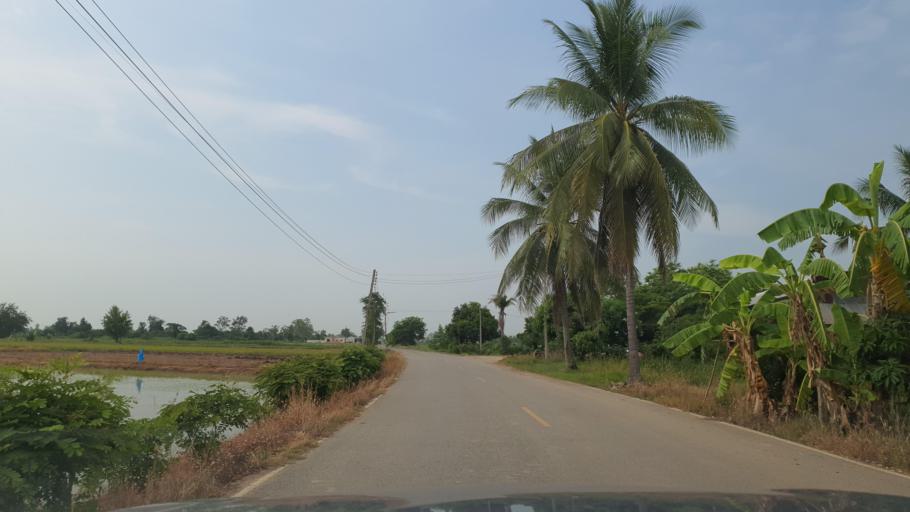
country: TH
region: Phitsanulok
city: Bang Rakam
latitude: 16.8079
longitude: 100.1621
